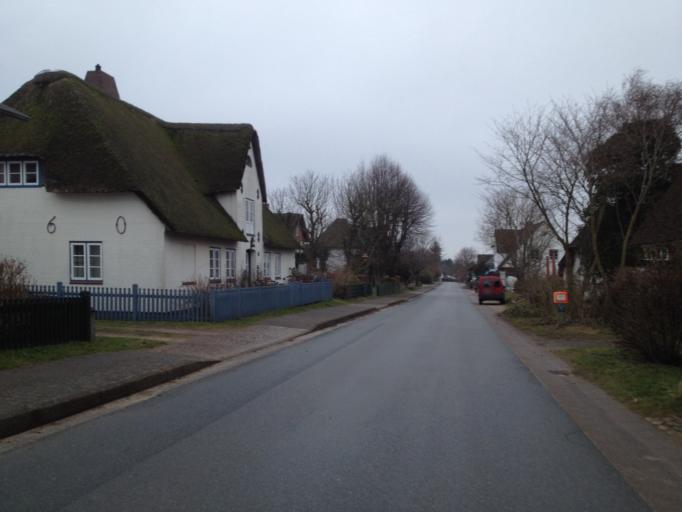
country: DE
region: Schleswig-Holstein
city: Nebel
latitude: 54.6511
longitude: 8.3537
